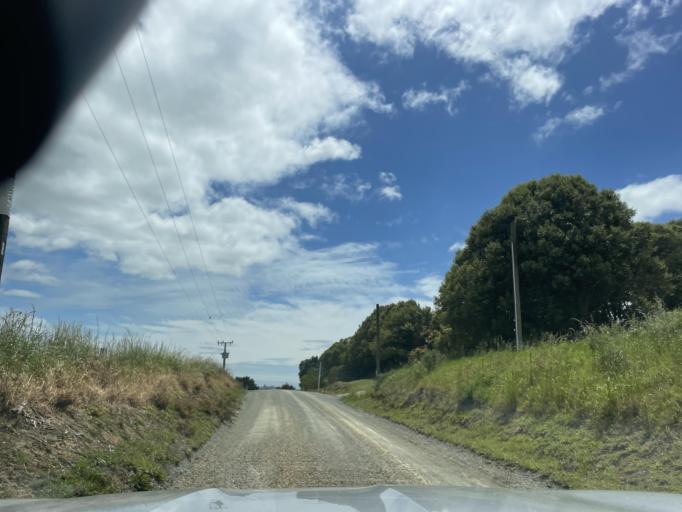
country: NZ
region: Auckland
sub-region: Auckland
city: Wellsford
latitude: -36.1555
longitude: 174.5427
